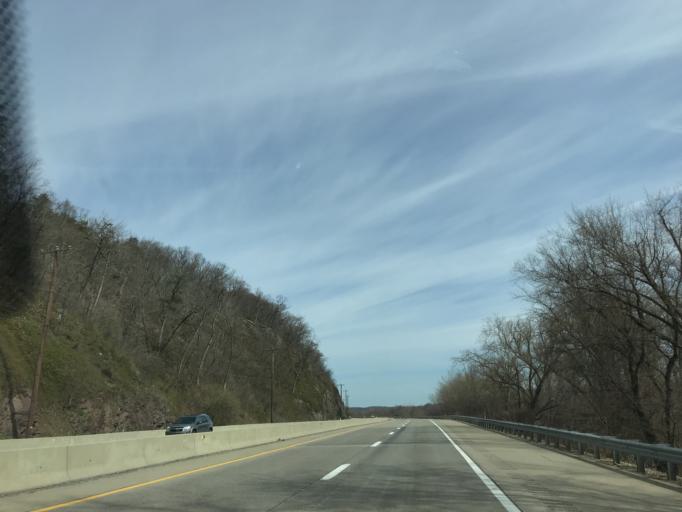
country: US
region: Pennsylvania
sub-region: Dauphin County
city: Millersburg
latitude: 40.6034
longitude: -76.9540
